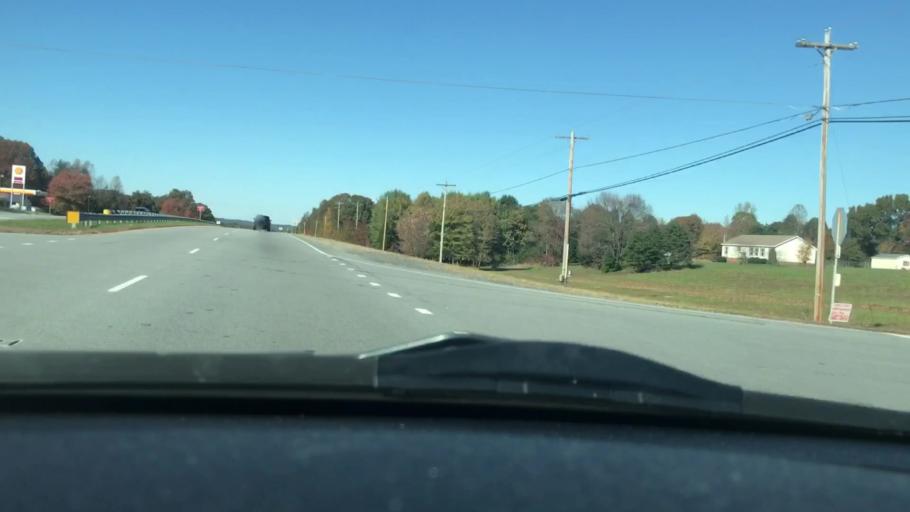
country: US
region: North Carolina
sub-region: Rockingham County
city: Madison
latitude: 36.3447
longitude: -79.9441
